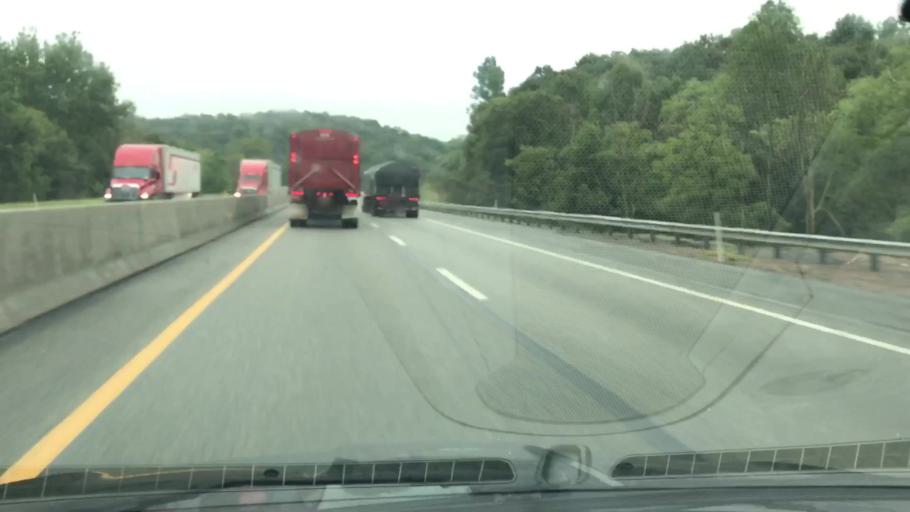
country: US
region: Pennsylvania
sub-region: Bedford County
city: Earlston
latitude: 40.0005
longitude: -78.3465
